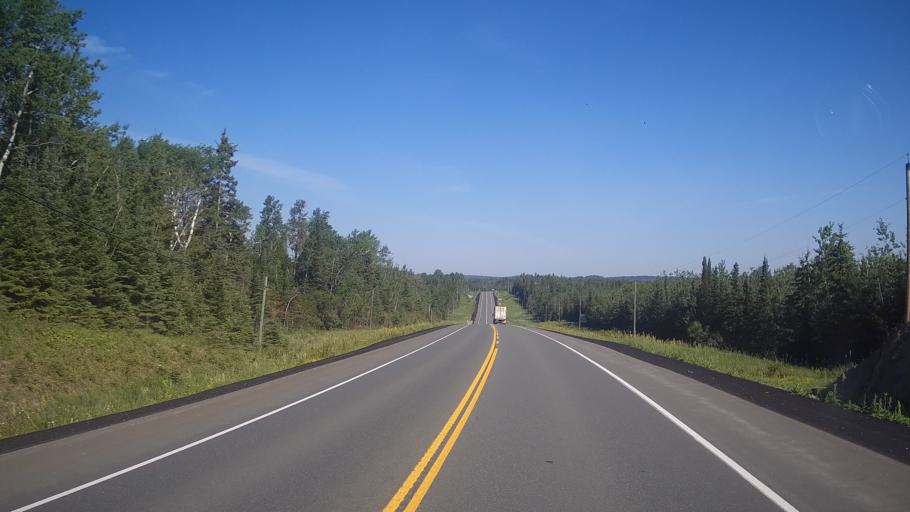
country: CA
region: Ontario
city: Dryden
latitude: 49.6627
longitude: -92.4831
